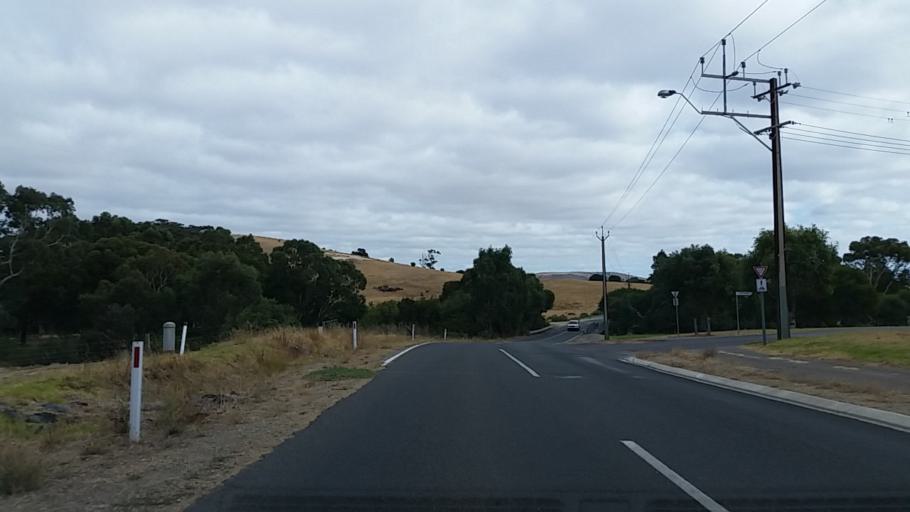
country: AU
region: South Australia
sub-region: Yankalilla
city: Normanville
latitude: -35.4309
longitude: 138.3253
